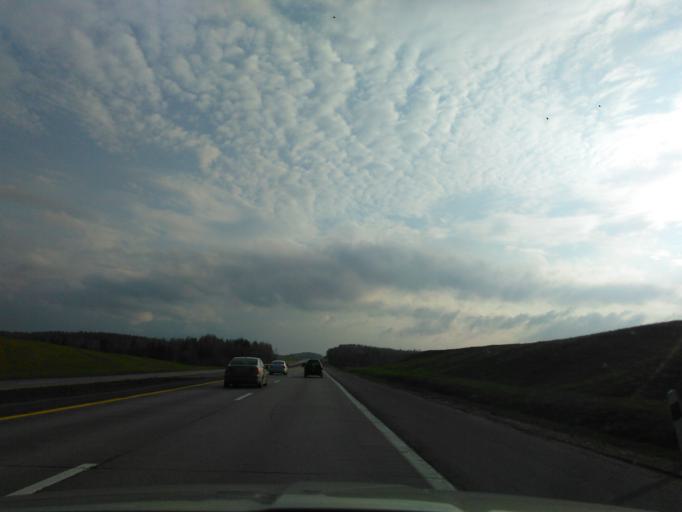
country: BY
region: Minsk
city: Astrashytski Haradok
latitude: 54.0787
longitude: 27.7421
